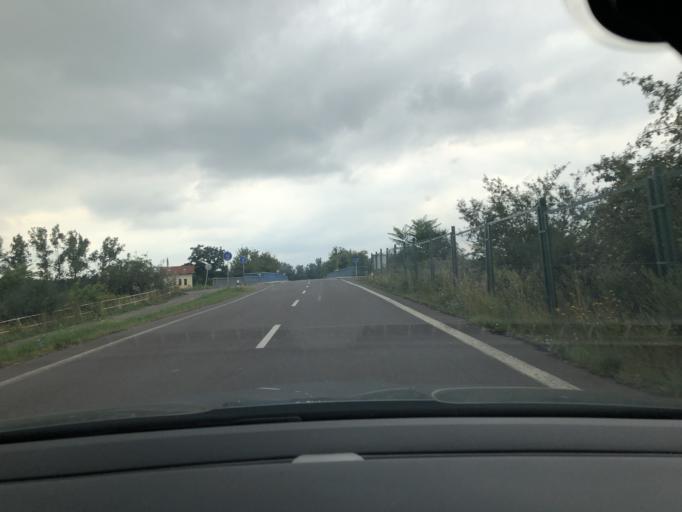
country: CZ
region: South Moravian
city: Hevlin
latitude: 48.7429
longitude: 16.3815
